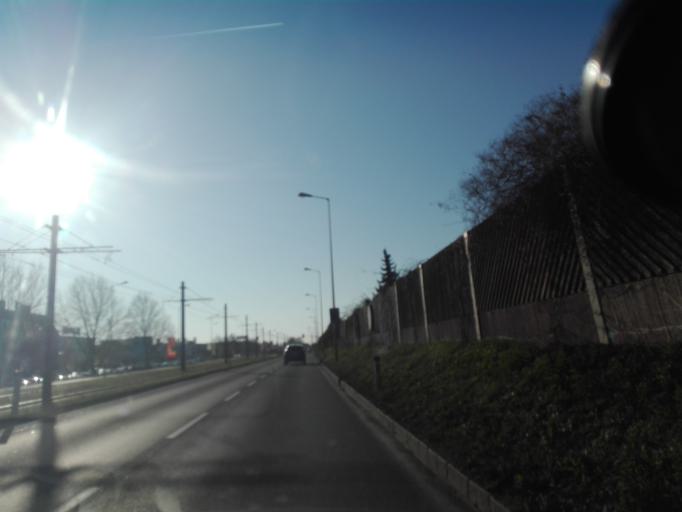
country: AT
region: Upper Austria
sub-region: Politischer Bezirk Linz-Land
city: Leonding
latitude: 48.2614
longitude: 14.2573
